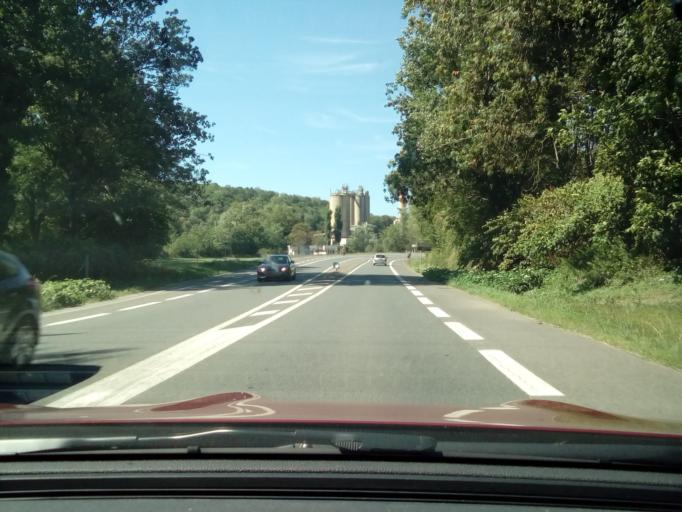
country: FR
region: Rhone-Alpes
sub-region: Departement du Rhone
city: Lozanne
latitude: 45.8621
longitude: 4.6646
